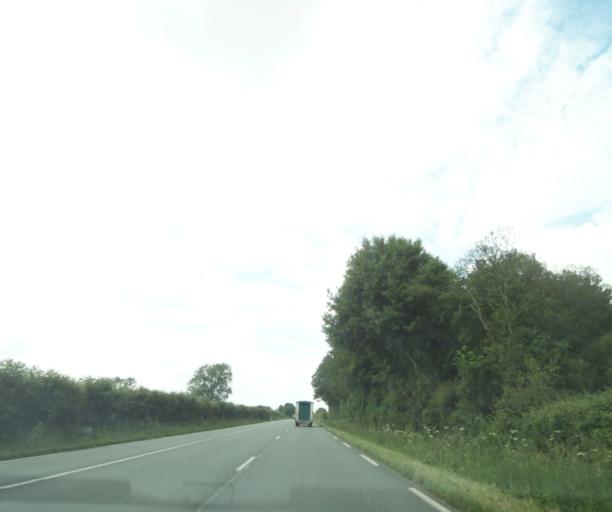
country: FR
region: Poitou-Charentes
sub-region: Departement des Deux-Sevres
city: Champdeniers-Saint-Denis
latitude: 46.5011
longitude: -0.3395
